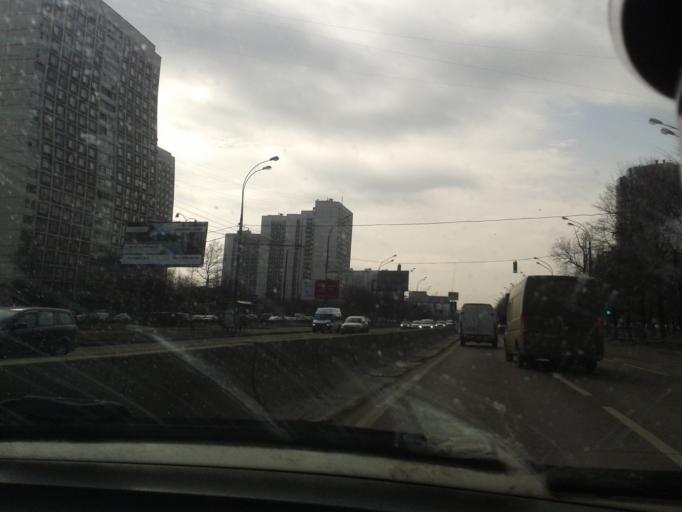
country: RU
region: Moscow
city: Lianozovo
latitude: 55.8945
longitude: 37.5867
